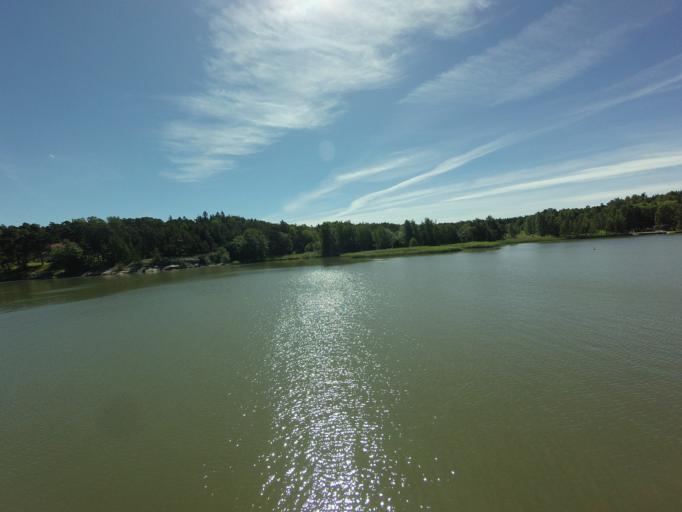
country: FI
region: Varsinais-Suomi
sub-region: Turku
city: Raisio
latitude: 60.4151
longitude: 22.1552
